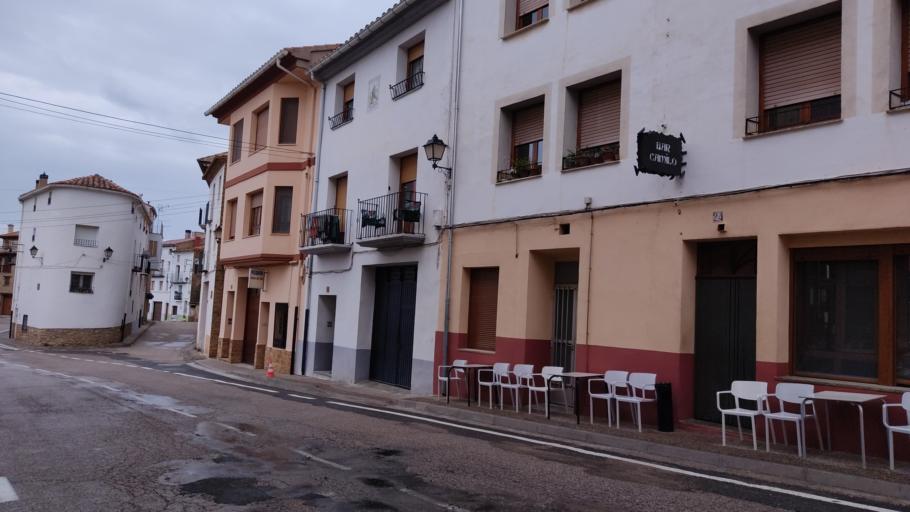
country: ES
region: Aragon
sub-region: Provincia de Teruel
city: La Iglesuela del Cid
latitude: 40.4810
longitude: -0.3192
